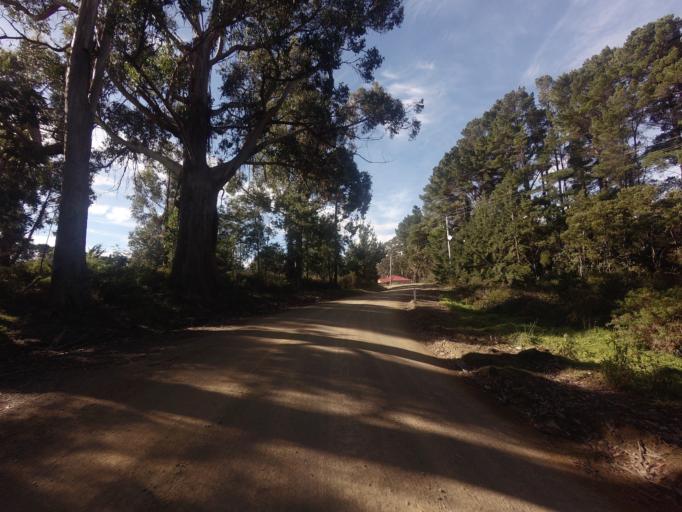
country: AU
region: Tasmania
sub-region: Clarence
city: Sandford
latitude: -43.1443
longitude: 147.7642
